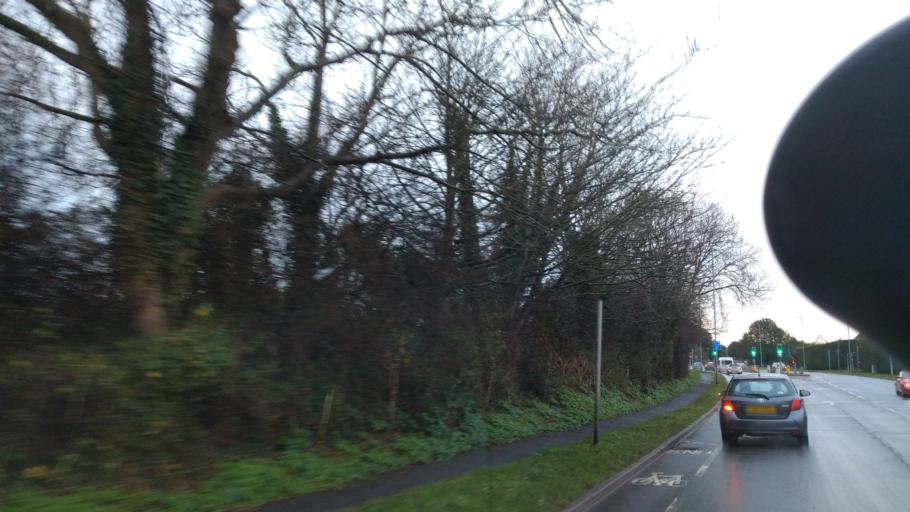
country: GB
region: England
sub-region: East Sussex
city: Eastbourne
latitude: 50.8055
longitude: 0.2493
